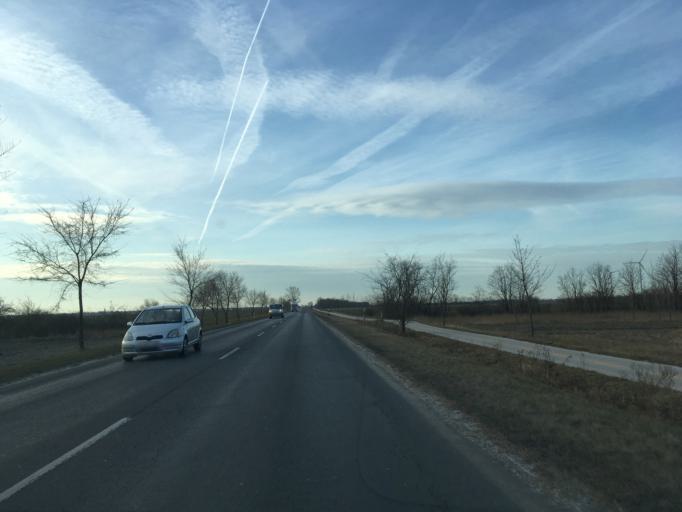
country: HU
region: Gyor-Moson-Sopron
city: Mosonmagyarovar
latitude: 47.8864
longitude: 17.2369
